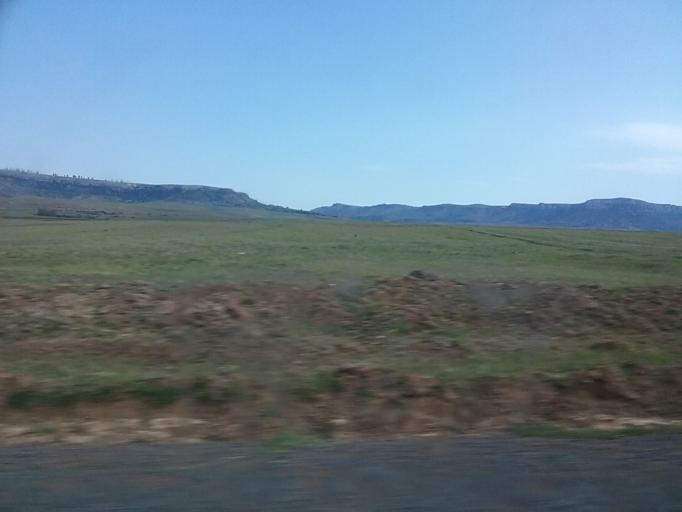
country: LS
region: Berea
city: Teyateyaneng
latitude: -29.0837
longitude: 27.9001
